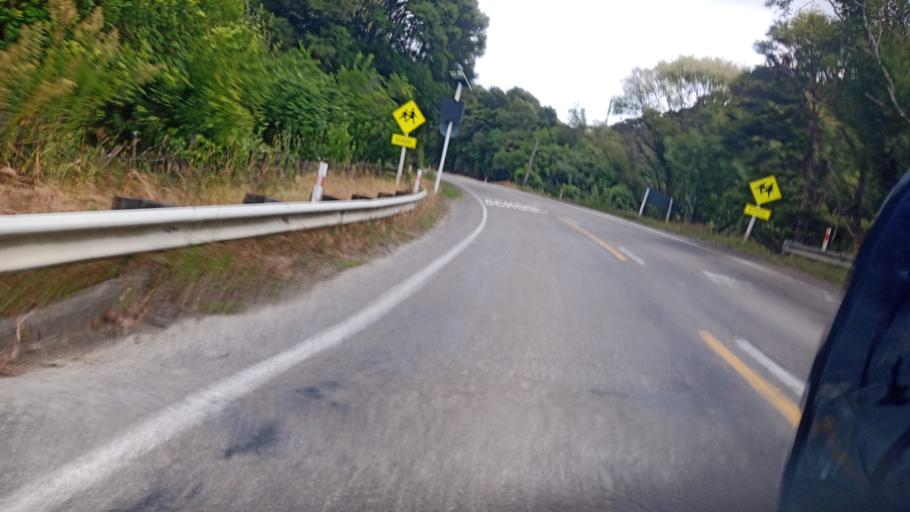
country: NZ
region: Gisborne
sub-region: Gisborne District
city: Gisborne
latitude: -38.2942
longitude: 178.2761
